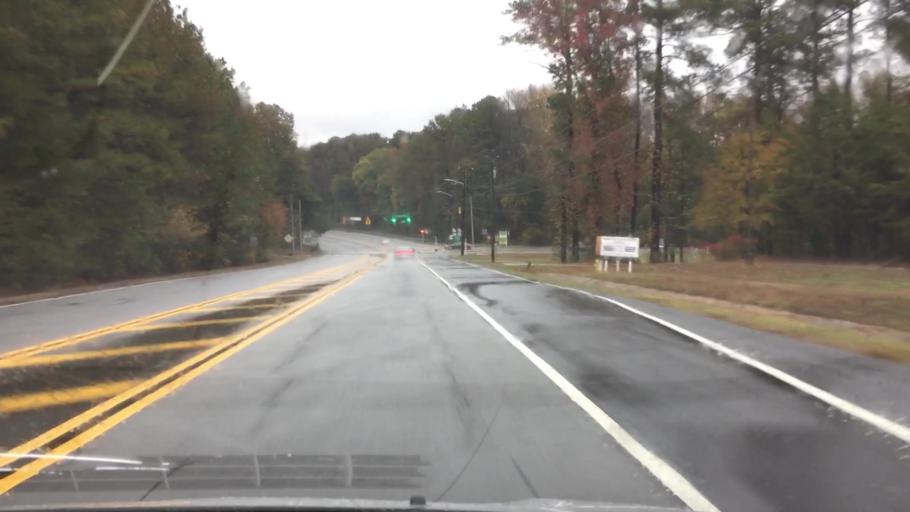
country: US
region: Georgia
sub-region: DeKalb County
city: Pine Mountain
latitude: 33.6779
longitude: -84.1957
